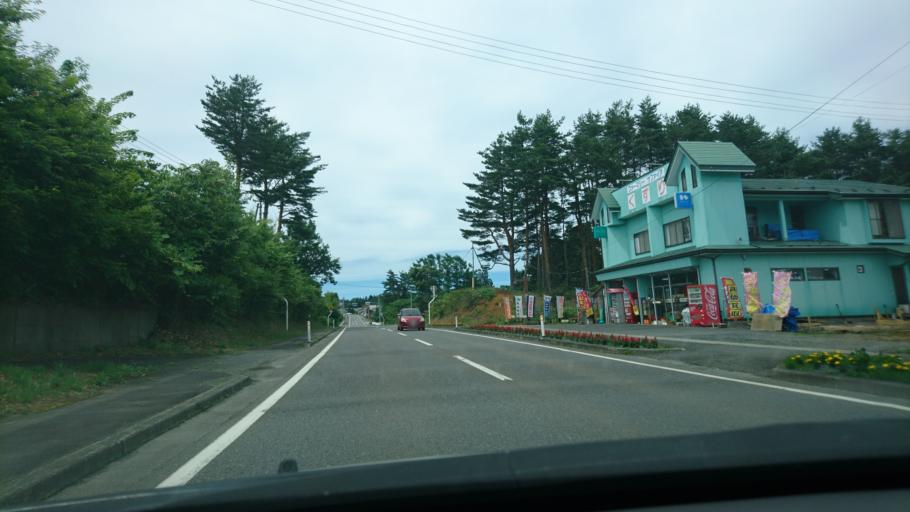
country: JP
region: Iwate
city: Miyako
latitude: 39.9207
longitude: 141.9028
